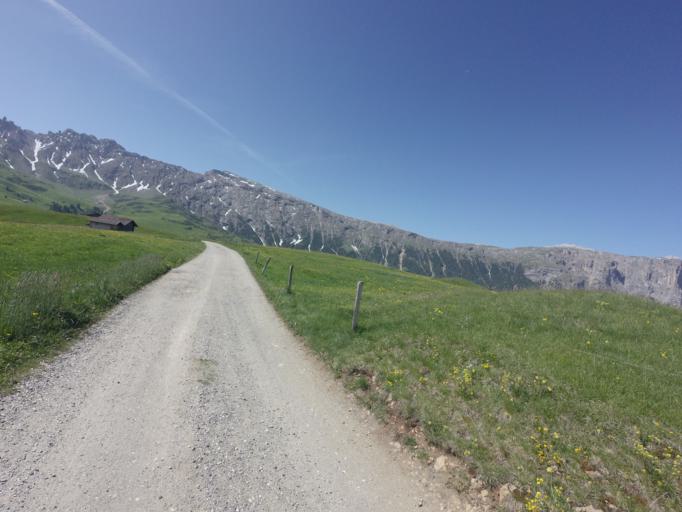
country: IT
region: Trentino-Alto Adige
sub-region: Bolzano
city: Siusi
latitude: 46.5269
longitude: 11.6217
